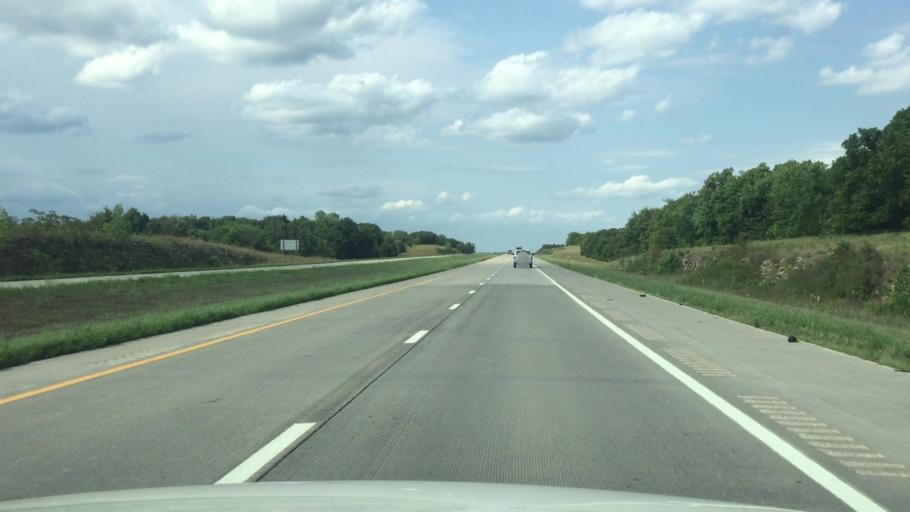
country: US
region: Kansas
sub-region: Miami County
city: Louisburg
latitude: 38.5785
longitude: -94.6957
